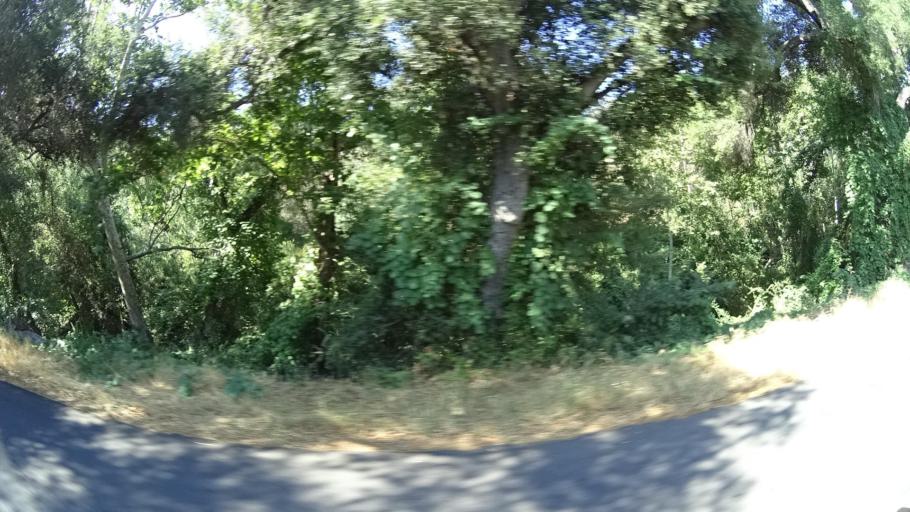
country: US
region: California
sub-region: San Diego County
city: Fallbrook
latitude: 33.4096
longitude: -117.2076
